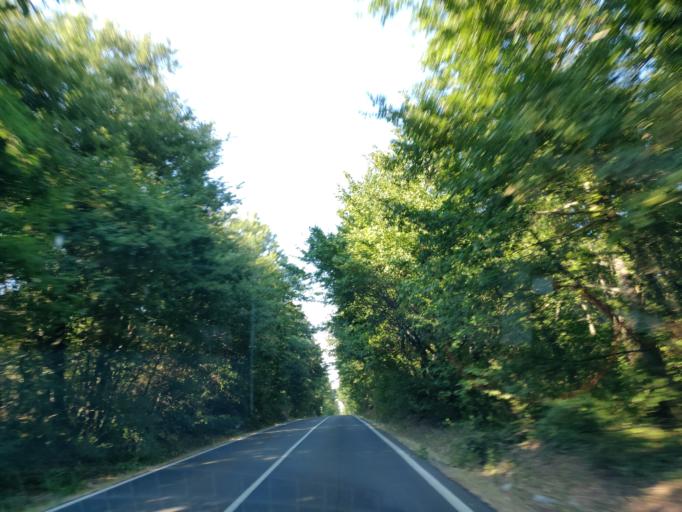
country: IT
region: Latium
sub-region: Provincia di Viterbo
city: Latera
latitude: 42.6016
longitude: 11.8418
